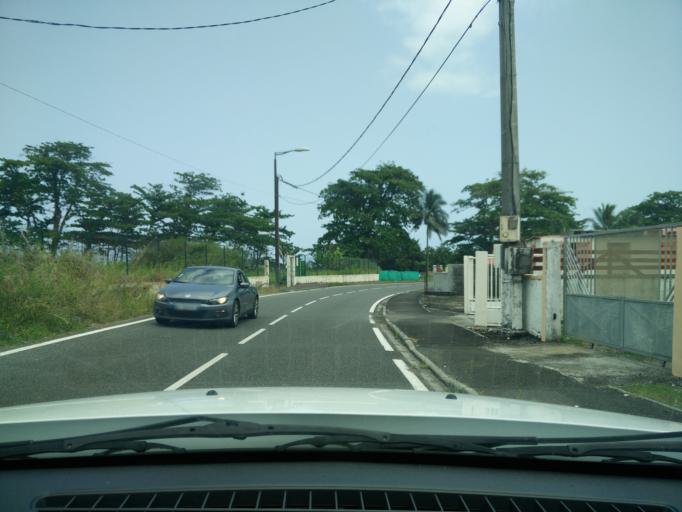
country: GP
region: Guadeloupe
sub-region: Guadeloupe
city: Capesterre-Belle-Eau
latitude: 16.0512
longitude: -61.5578
